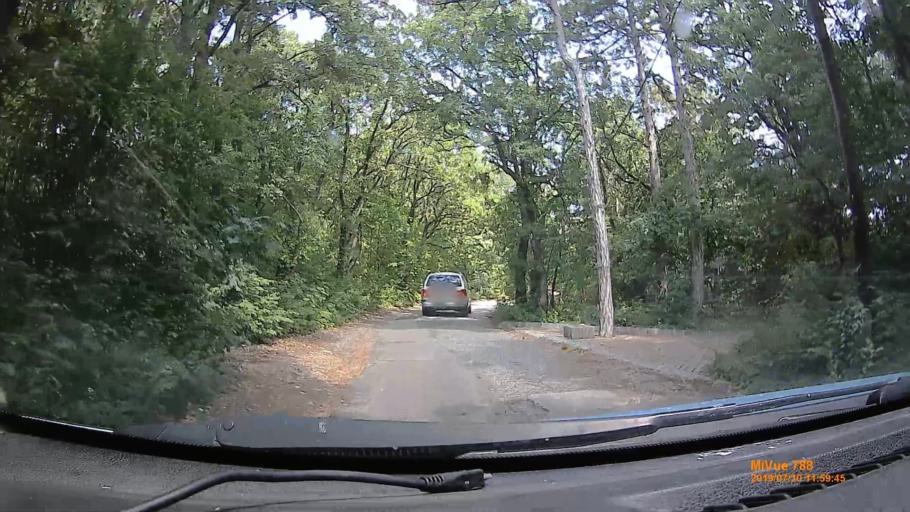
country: HU
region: Baranya
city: Pecs
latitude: 46.0904
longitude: 18.2158
